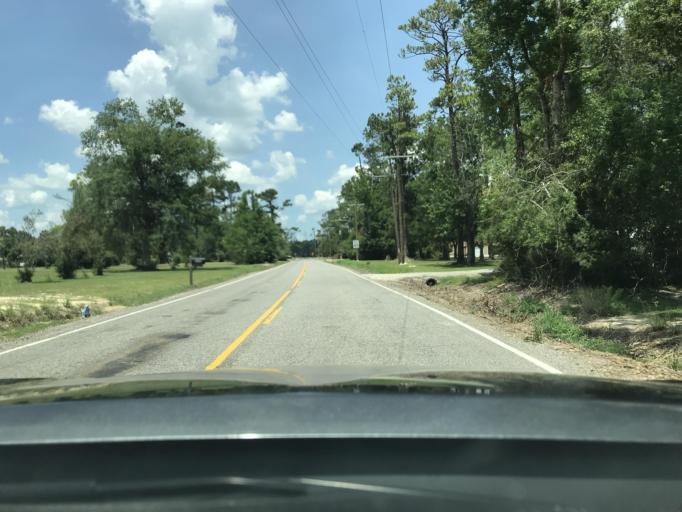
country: US
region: Louisiana
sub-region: Calcasieu Parish
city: Moss Bluff
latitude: 30.3224
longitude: -93.1766
